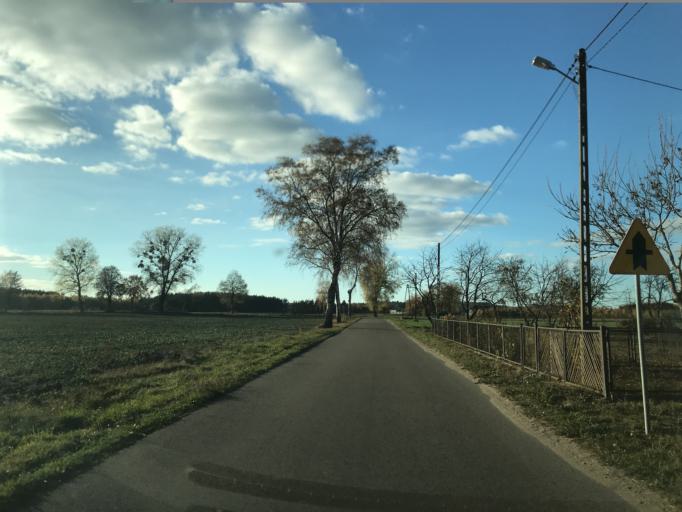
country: PL
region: Warmian-Masurian Voivodeship
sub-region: Powiat dzialdowski
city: Rybno
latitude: 53.3741
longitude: 19.8339
